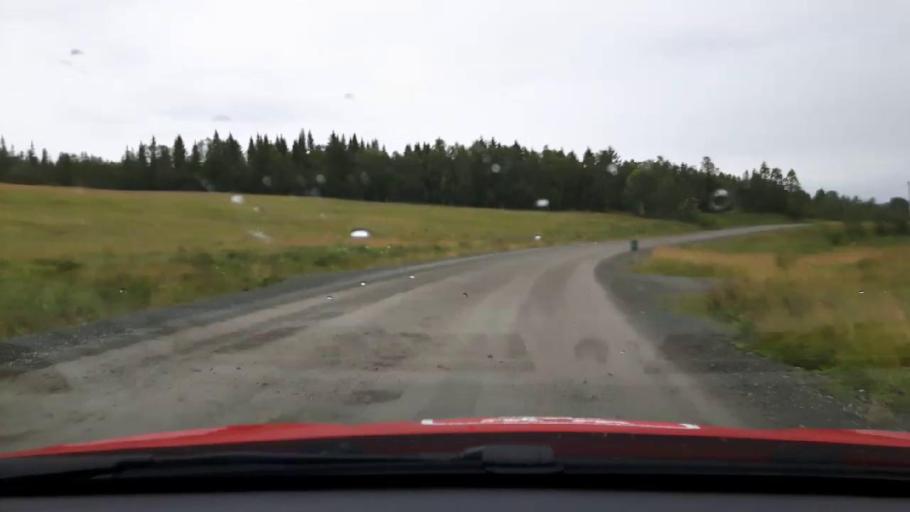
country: SE
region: Jaemtland
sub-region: Are Kommun
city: Are
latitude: 63.4615
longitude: 12.6338
